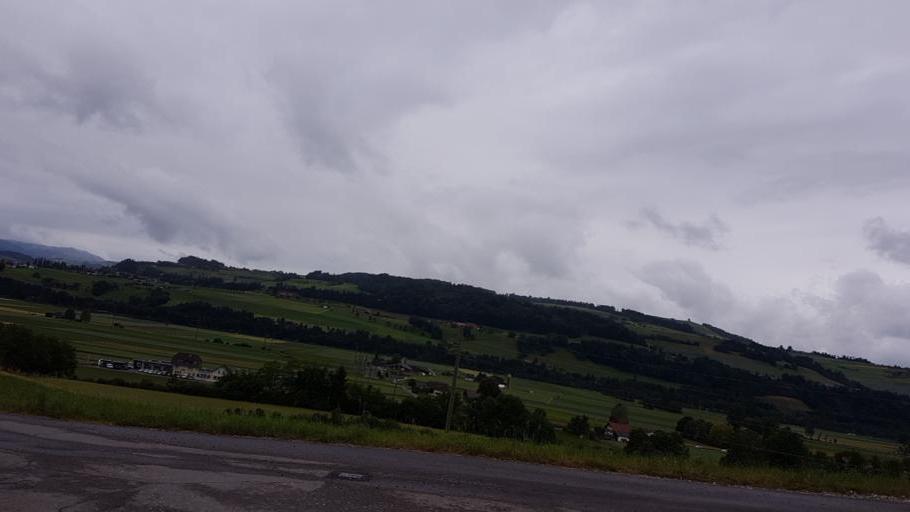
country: CH
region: Bern
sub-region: Bern-Mittelland District
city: Niederwichtrach
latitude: 46.8559
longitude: 7.5772
